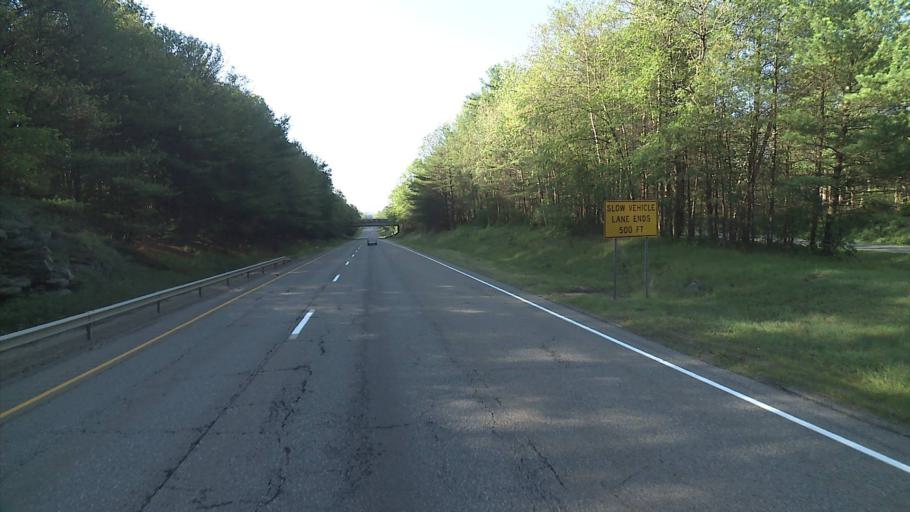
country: US
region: Connecticut
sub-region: Windham County
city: Killingly Center
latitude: 41.8689
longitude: -71.8909
